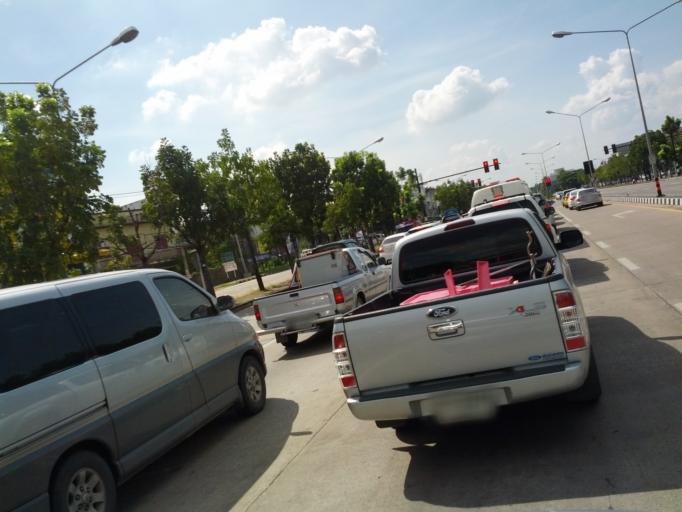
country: TH
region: Lampang
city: Lampang
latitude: 18.2816
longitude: 99.5006
